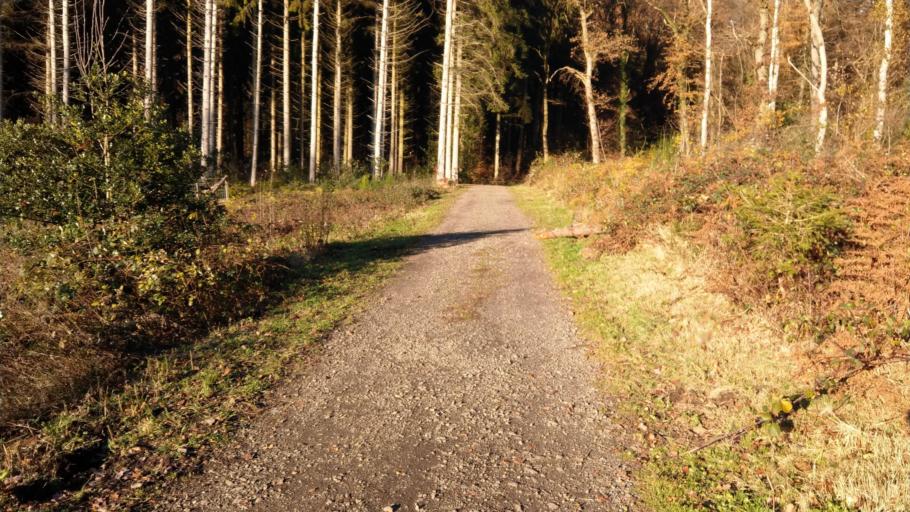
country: BE
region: Wallonia
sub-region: Province de Liege
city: La Calamine
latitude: 50.7321
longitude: 6.0101
